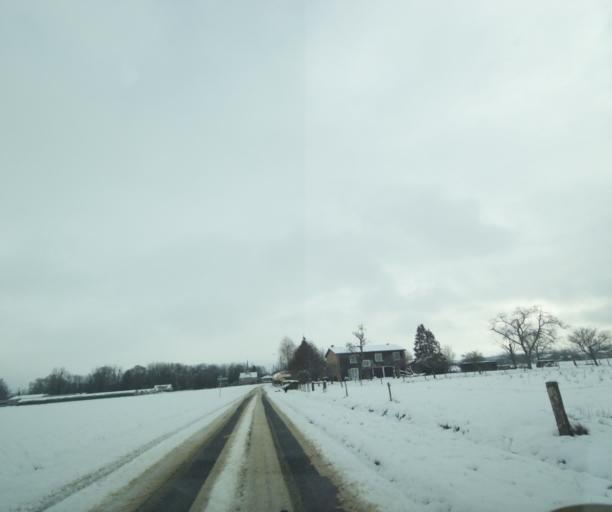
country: FR
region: Champagne-Ardenne
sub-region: Departement de la Haute-Marne
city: Montier-en-Der
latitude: 48.4968
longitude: 4.6954
